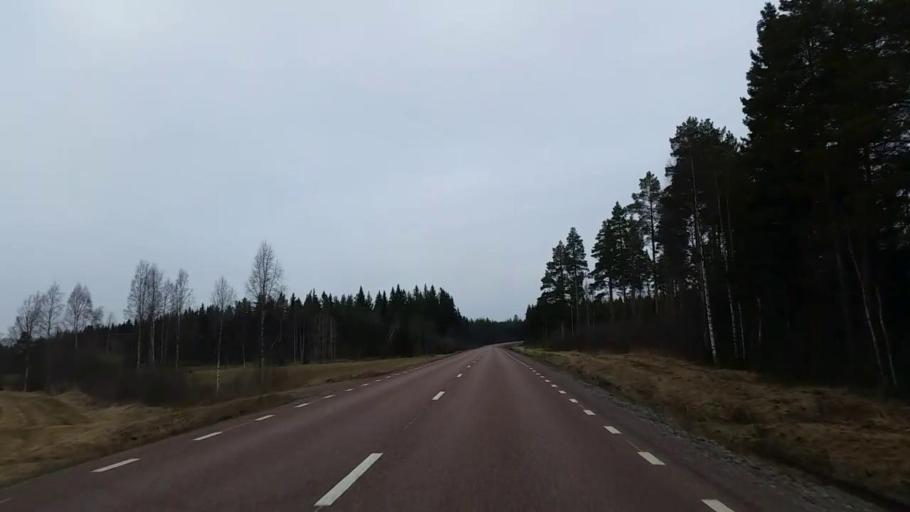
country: SE
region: Gaevleborg
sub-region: Ovanakers Kommun
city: Edsbyn
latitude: 61.2740
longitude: 15.8944
